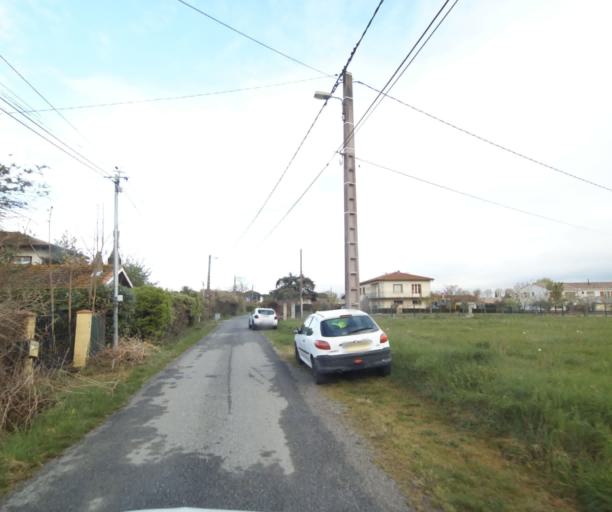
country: FR
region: Midi-Pyrenees
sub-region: Departement de l'Ariege
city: Saverdun
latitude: 43.2287
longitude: 1.5851
